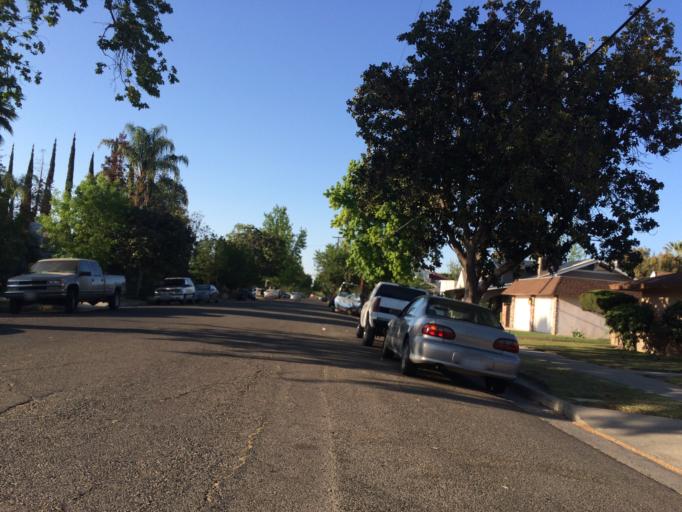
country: US
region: California
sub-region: Fresno County
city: Fresno
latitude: 36.7581
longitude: -119.7978
